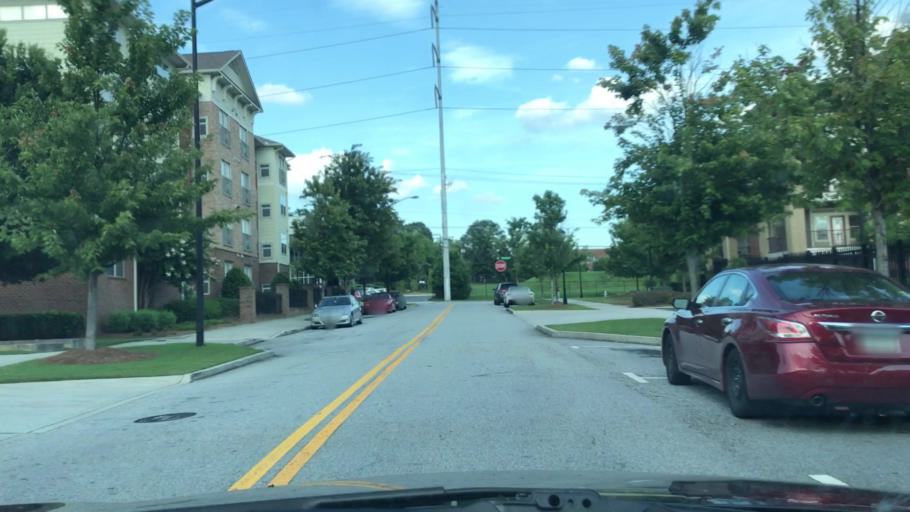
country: US
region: Georgia
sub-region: Fulton County
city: Atlanta
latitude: 33.7512
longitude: -84.3776
